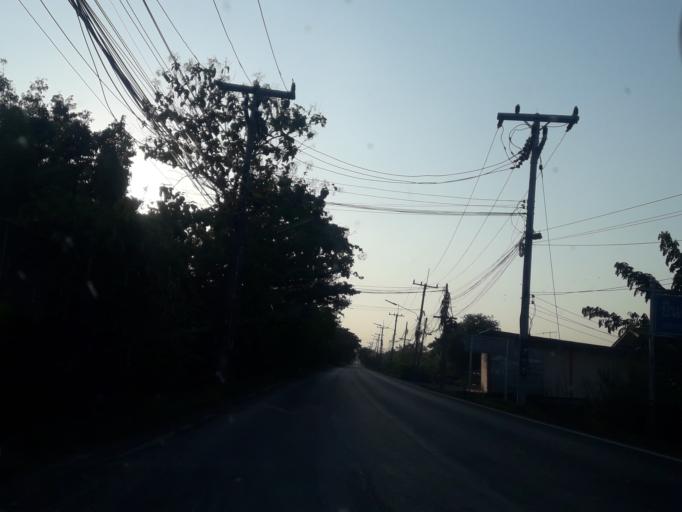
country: TH
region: Pathum Thani
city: Nong Suea
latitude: 14.1317
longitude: 100.8120
